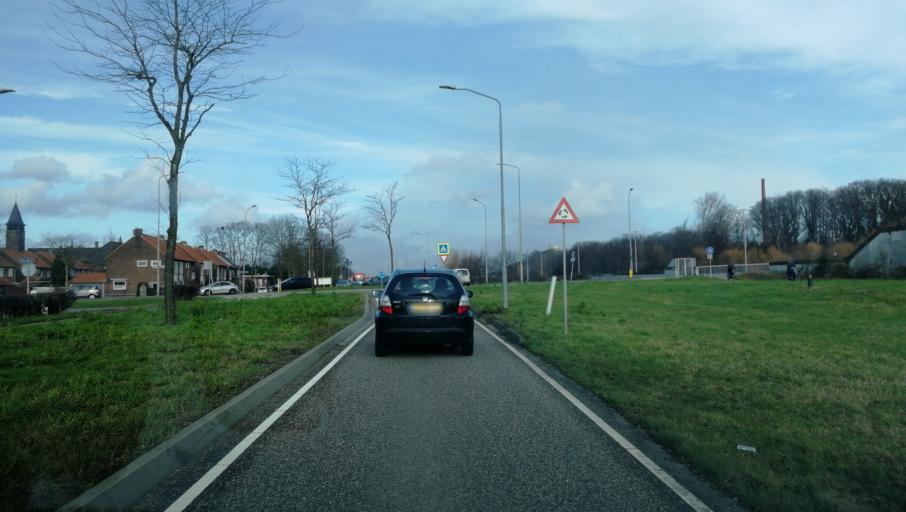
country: NL
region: Limburg
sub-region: Gemeente Venlo
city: Tegelen
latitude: 51.3342
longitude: 6.1474
